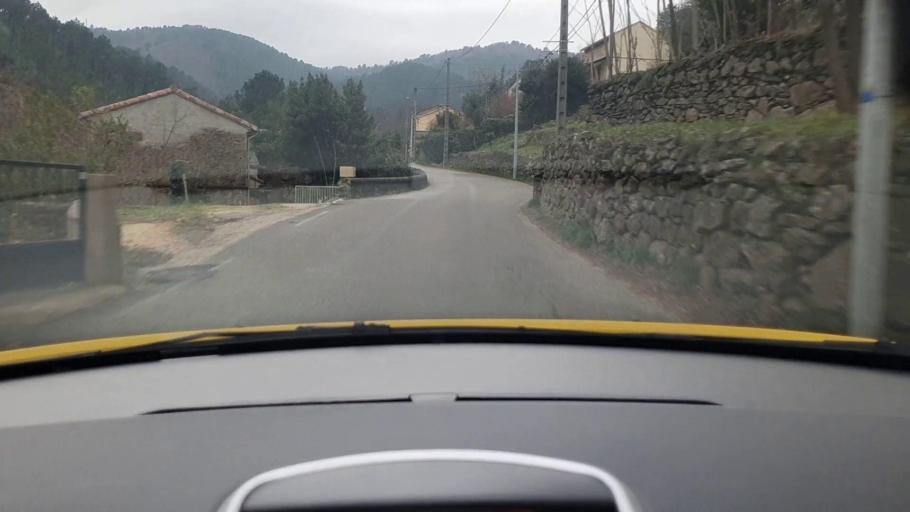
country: FR
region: Languedoc-Roussillon
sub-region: Departement du Gard
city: Besseges
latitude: 44.2784
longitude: 4.0831
